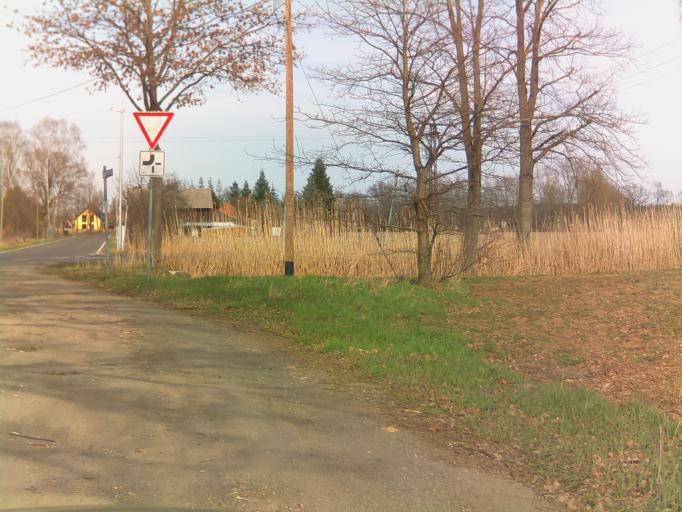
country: DE
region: Brandenburg
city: Cottbus
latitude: 51.8125
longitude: 14.3324
